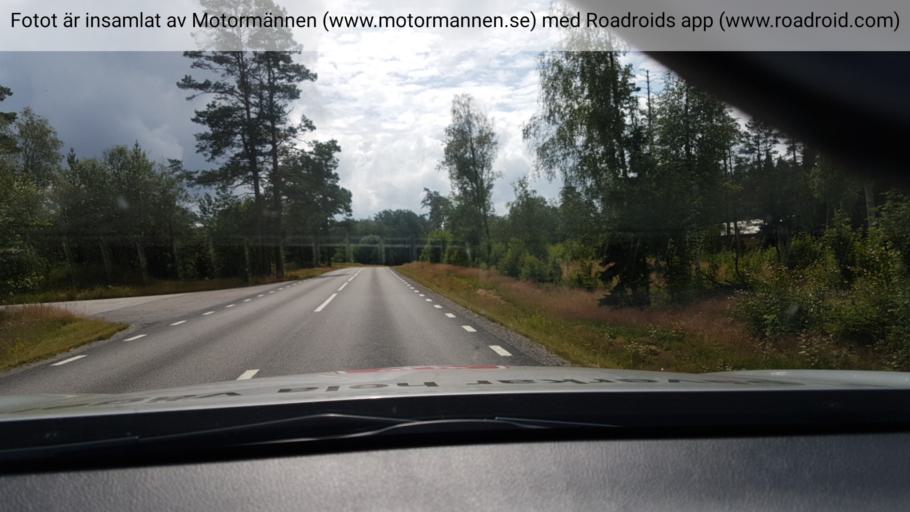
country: SE
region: Vaestra Goetaland
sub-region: Svenljunga Kommun
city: Svenljunga
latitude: 57.4689
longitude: 13.1694
